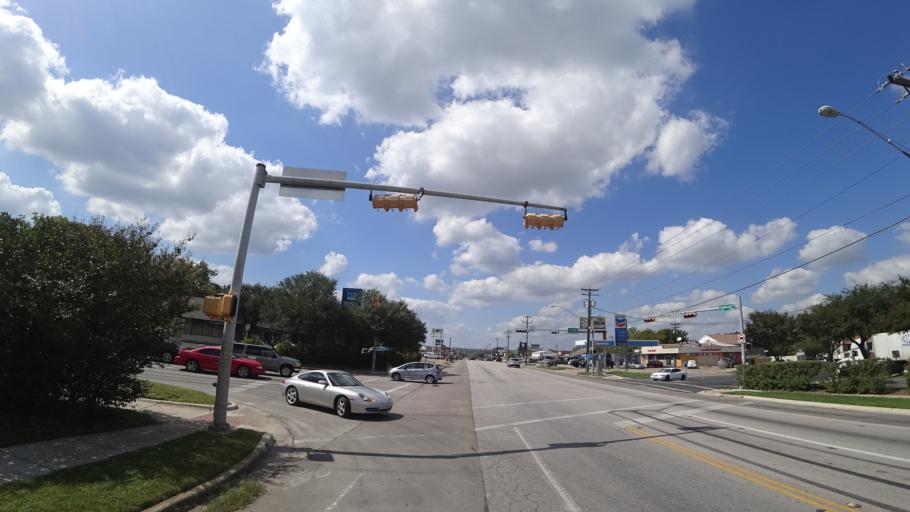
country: US
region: Texas
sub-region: Travis County
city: Austin
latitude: 30.3523
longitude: -97.7230
